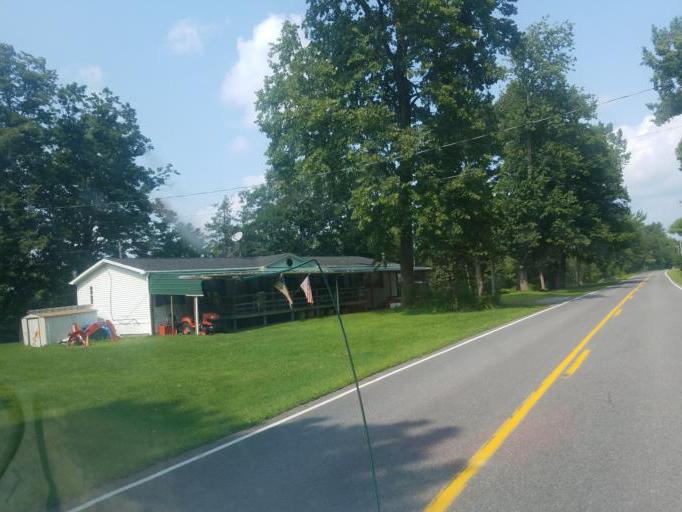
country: US
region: New York
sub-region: Montgomery County
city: Tribes Hill
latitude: 42.9188
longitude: -74.3243
